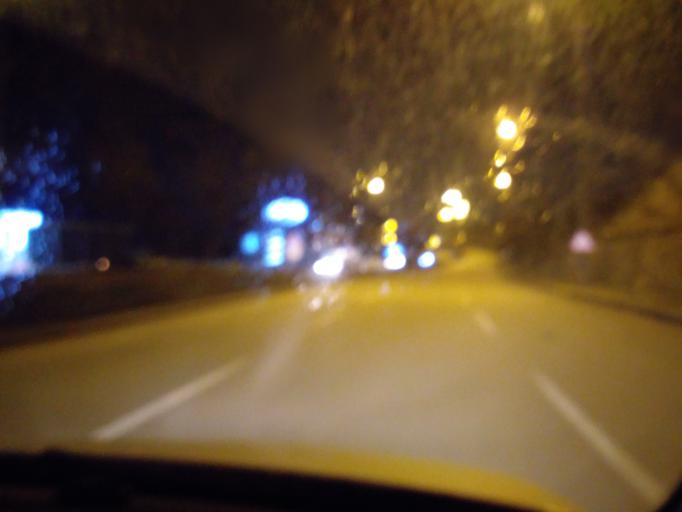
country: TR
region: Ankara
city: Batikent
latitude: 39.8863
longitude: 32.7169
